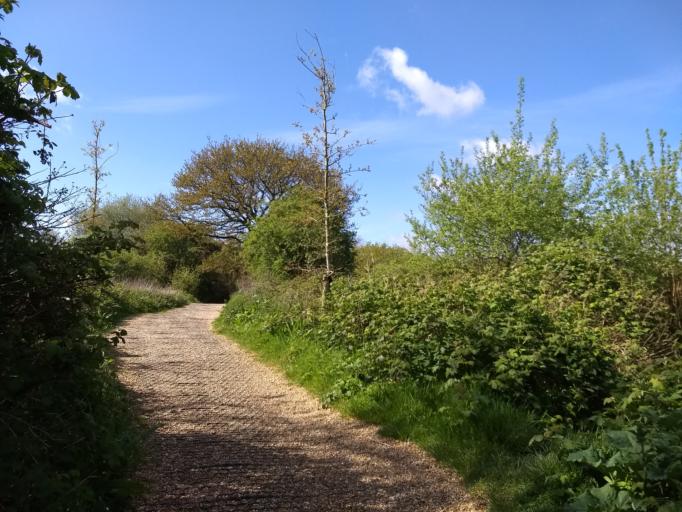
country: GB
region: England
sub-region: Isle of Wight
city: Newport
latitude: 50.7144
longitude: -1.2857
